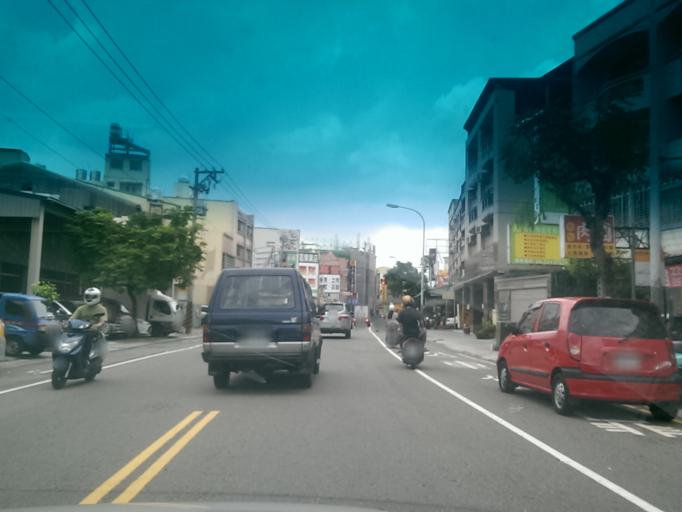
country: TW
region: Taiwan
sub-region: Taichung City
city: Taichung
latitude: 24.1389
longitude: 120.7029
